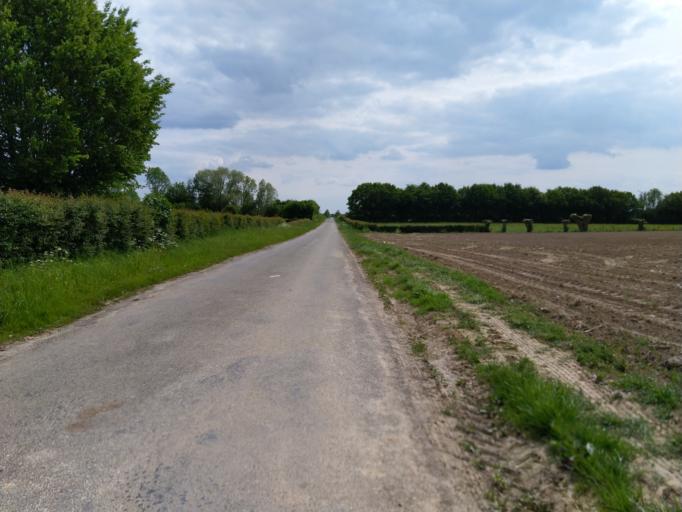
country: FR
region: Picardie
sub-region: Departement de l'Aisne
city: Boue
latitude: 50.0360
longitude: 3.6810
